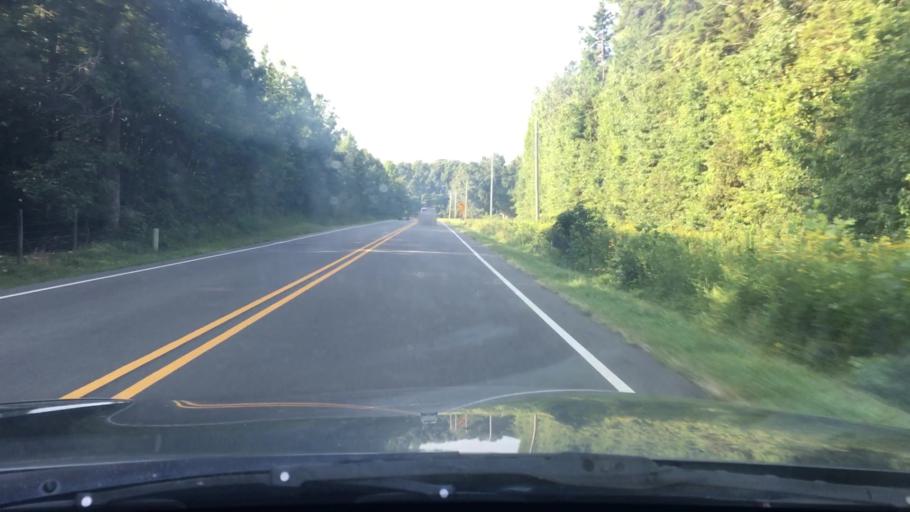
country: US
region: North Carolina
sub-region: Caswell County
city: Yanceyville
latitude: 36.2944
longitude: -79.3680
